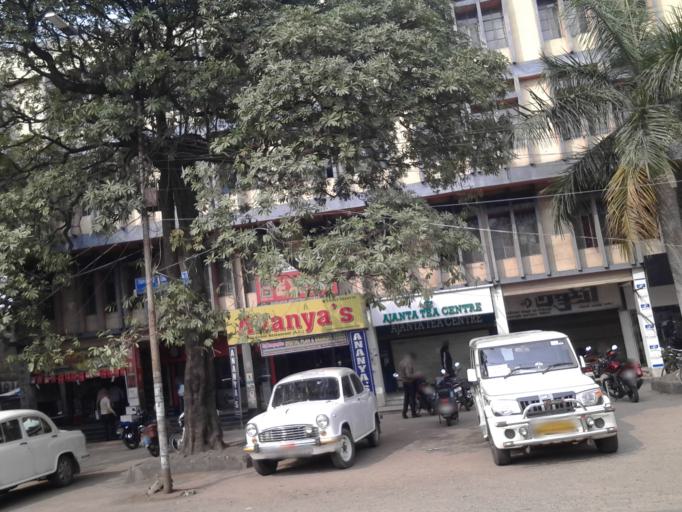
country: IN
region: West Bengal
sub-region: Barddhaman
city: Durgapur
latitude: 23.5371
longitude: 87.2966
